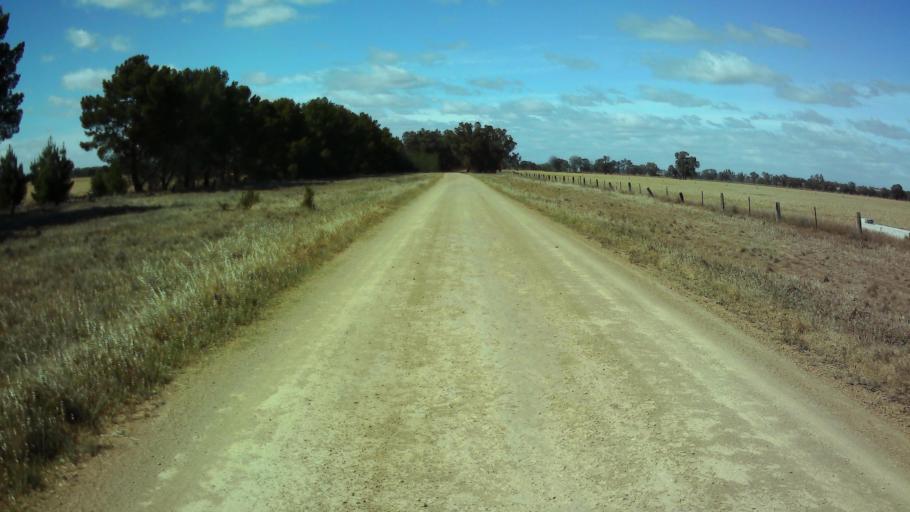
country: AU
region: New South Wales
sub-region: Weddin
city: Grenfell
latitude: -34.0336
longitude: 148.3169
